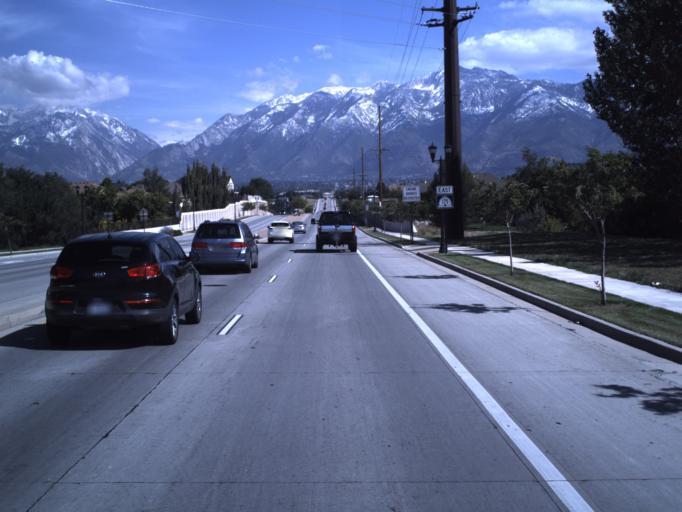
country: US
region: Utah
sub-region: Salt Lake County
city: South Jordan
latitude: 40.5441
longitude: -111.9287
